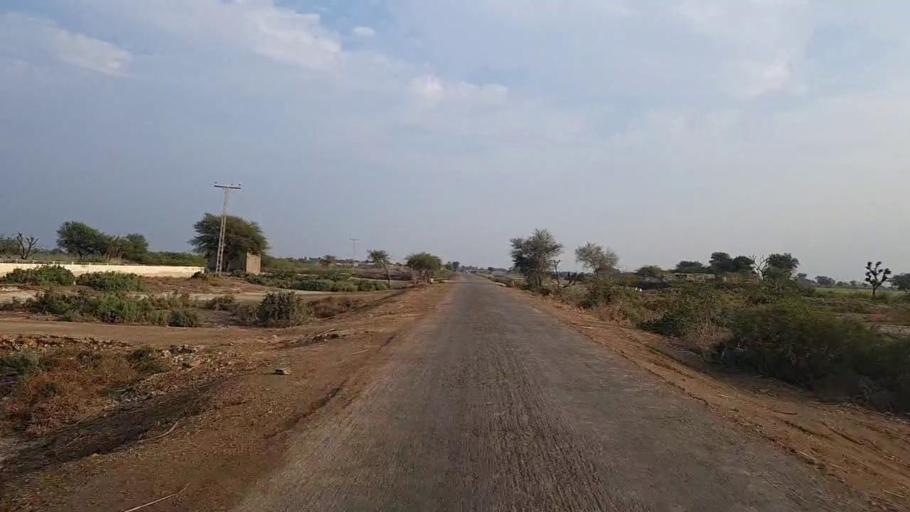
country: PK
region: Sindh
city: Pithoro
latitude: 25.4482
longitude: 69.2894
